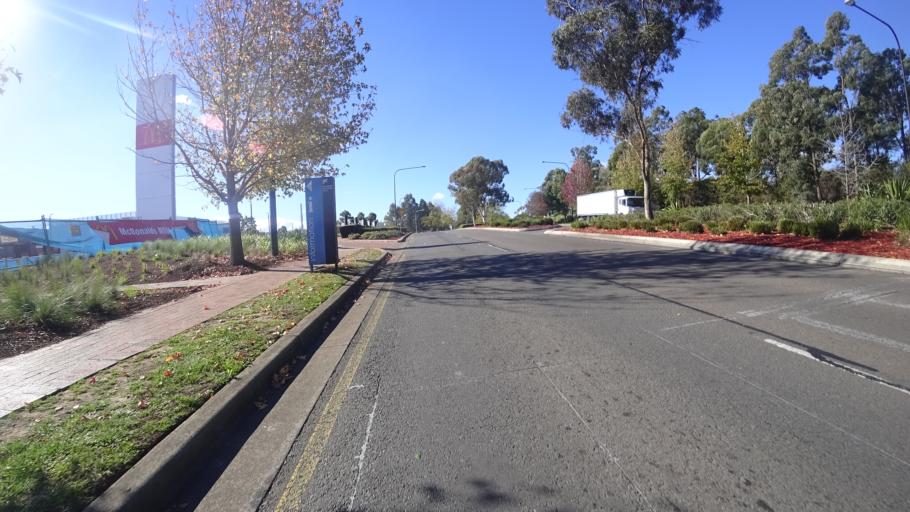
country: AU
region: New South Wales
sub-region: Blacktown
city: Stanhope Gardens
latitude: -33.7392
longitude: 150.9491
